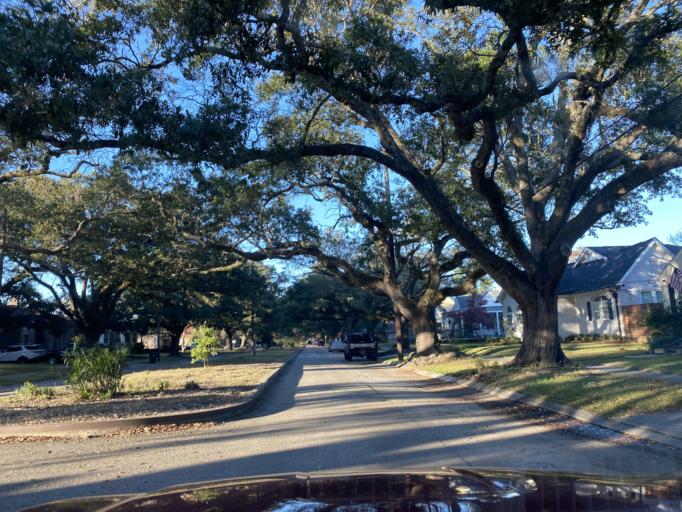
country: US
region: Louisiana
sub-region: Orleans Parish
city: New Orleans
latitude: 30.0075
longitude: -90.0553
